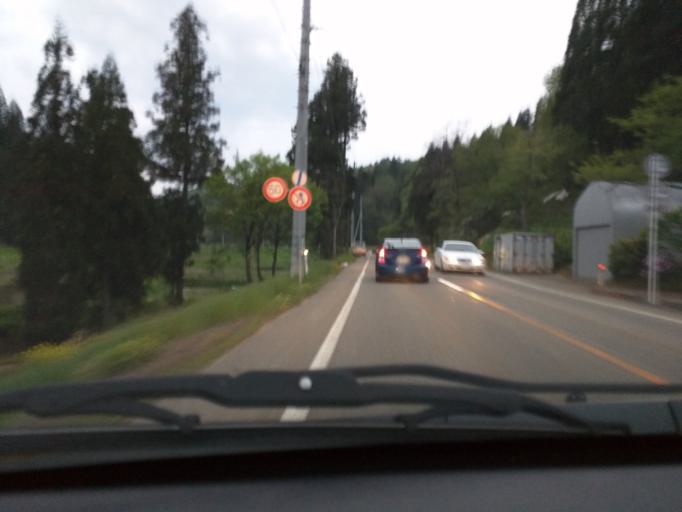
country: JP
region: Niigata
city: Ojiya
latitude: 37.3196
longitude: 138.6978
